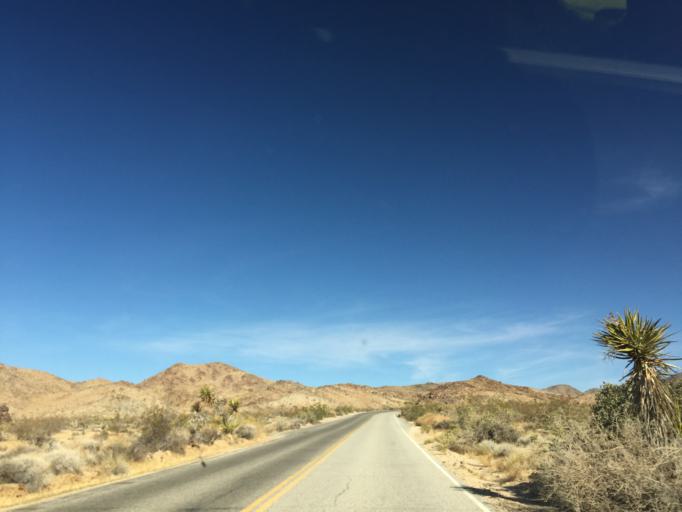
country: US
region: California
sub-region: San Bernardino County
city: Twentynine Palms
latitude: 33.9563
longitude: -115.9855
